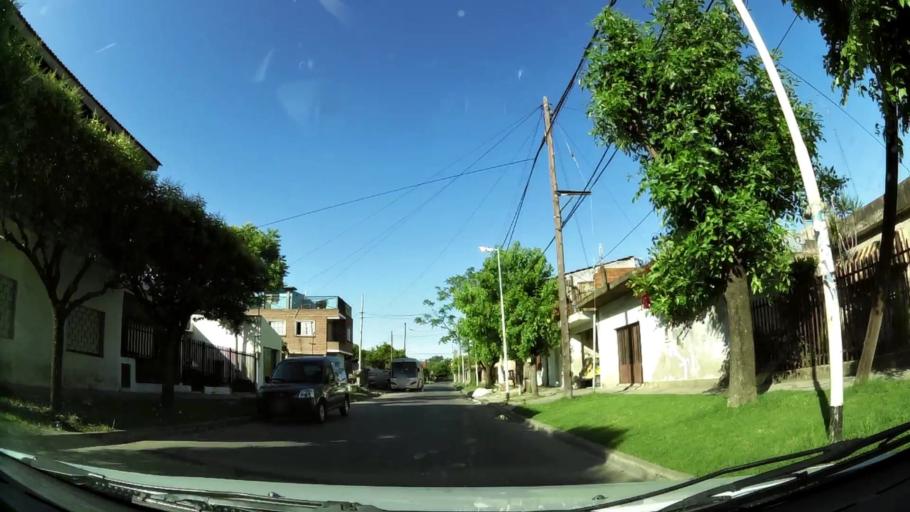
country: AR
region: Buenos Aires
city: Hurlingham
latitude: -34.5672
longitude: -58.6109
